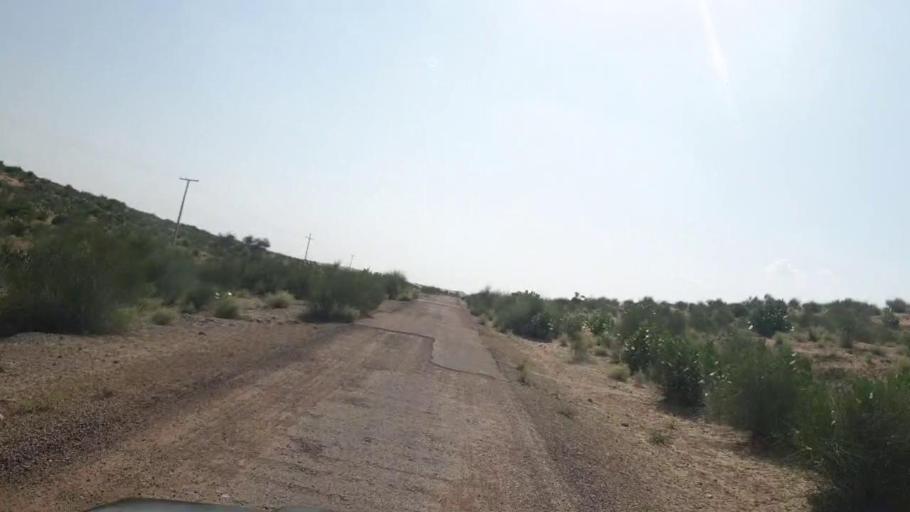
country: PK
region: Sindh
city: Chor
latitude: 25.5588
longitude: 70.2236
